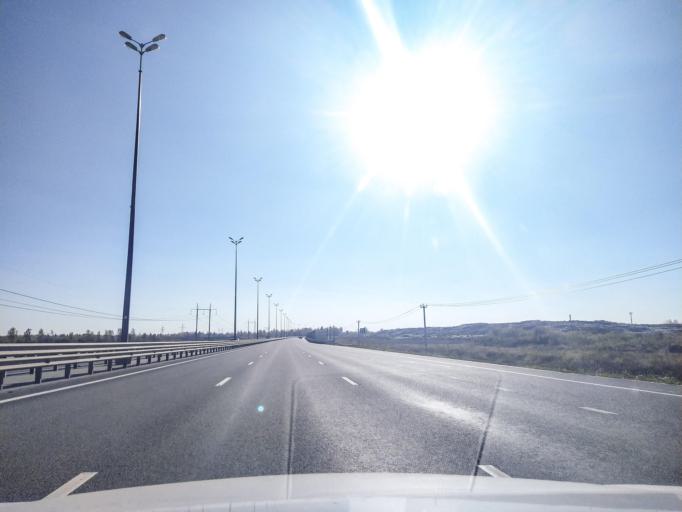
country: RU
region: Leningrad
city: Maloye Verevo
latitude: 59.5926
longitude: 30.1801
